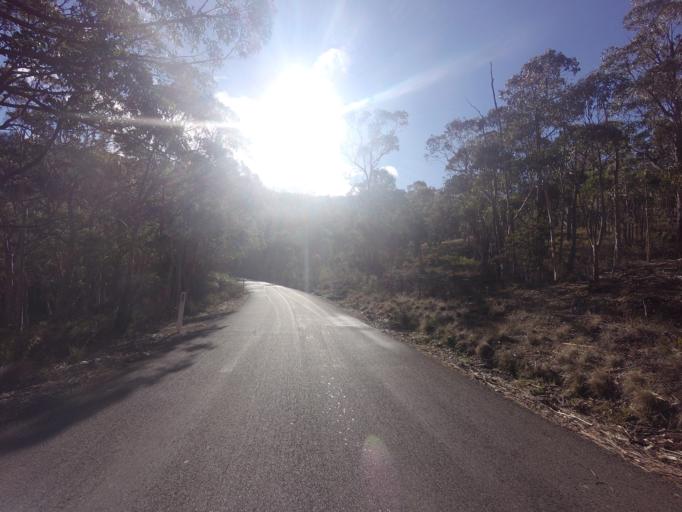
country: AU
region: Tasmania
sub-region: Glenorchy
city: Berriedale
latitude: -42.8211
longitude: 147.1926
